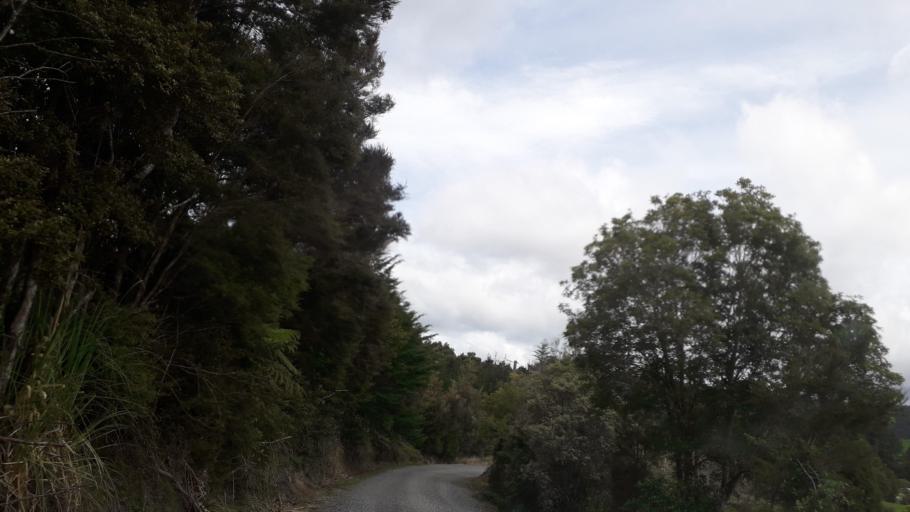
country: NZ
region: Northland
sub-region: Far North District
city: Waimate North
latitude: -35.1458
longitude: 173.7130
